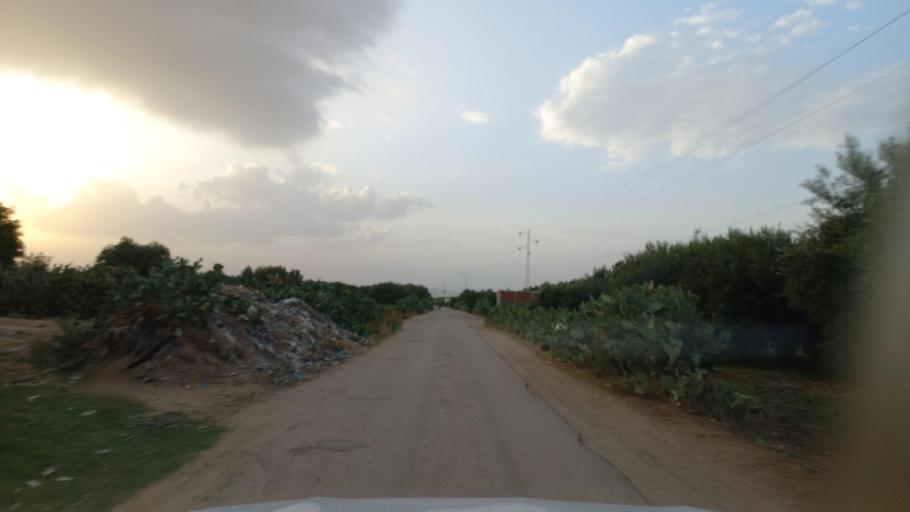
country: TN
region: Al Qasrayn
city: Kasserine
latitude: 35.2692
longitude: 9.0580
